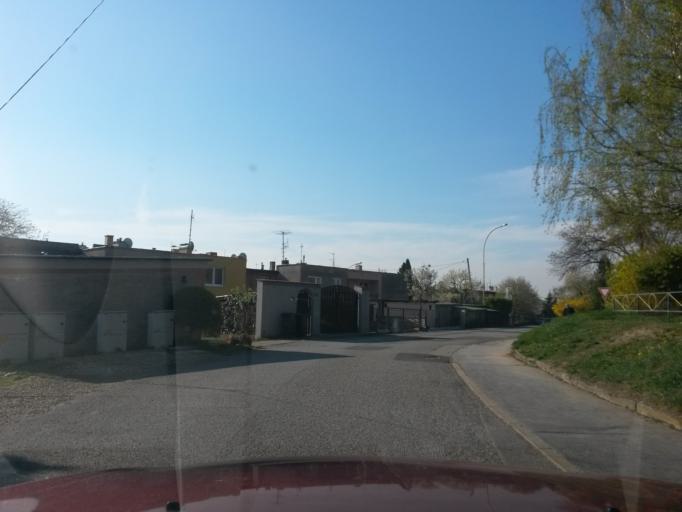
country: SK
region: Kosicky
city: Kosice
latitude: 48.7514
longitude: 21.2459
